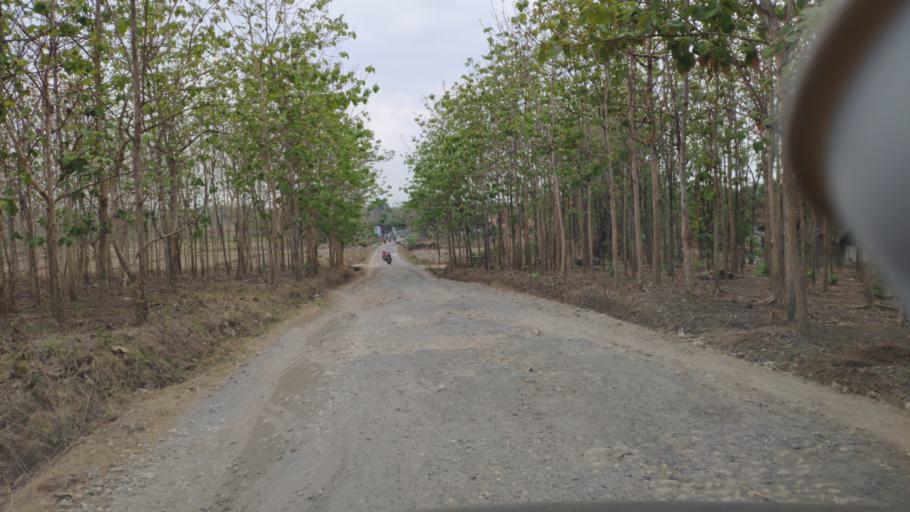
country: ID
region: Central Java
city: Jembangan
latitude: -6.9524
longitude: 111.3866
